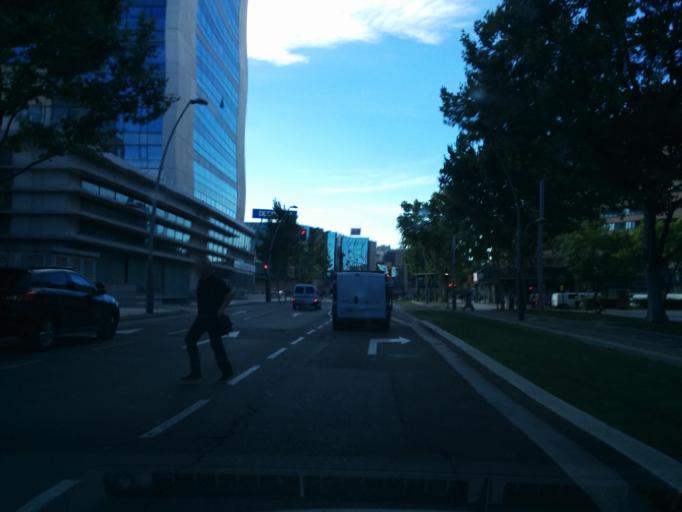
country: ES
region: Aragon
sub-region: Provincia de Zaragoza
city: Almozara
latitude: 41.6685
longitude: -0.8878
